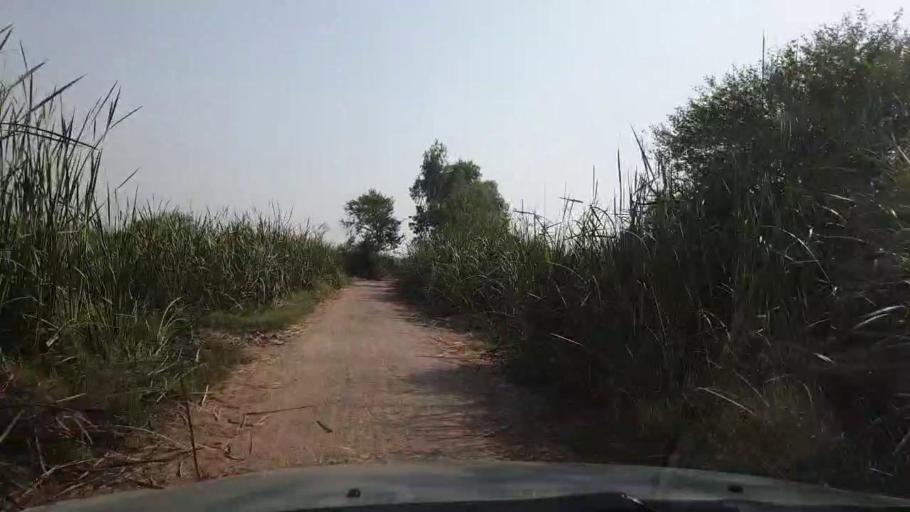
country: PK
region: Sindh
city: Bulri
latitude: 24.9014
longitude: 68.3763
